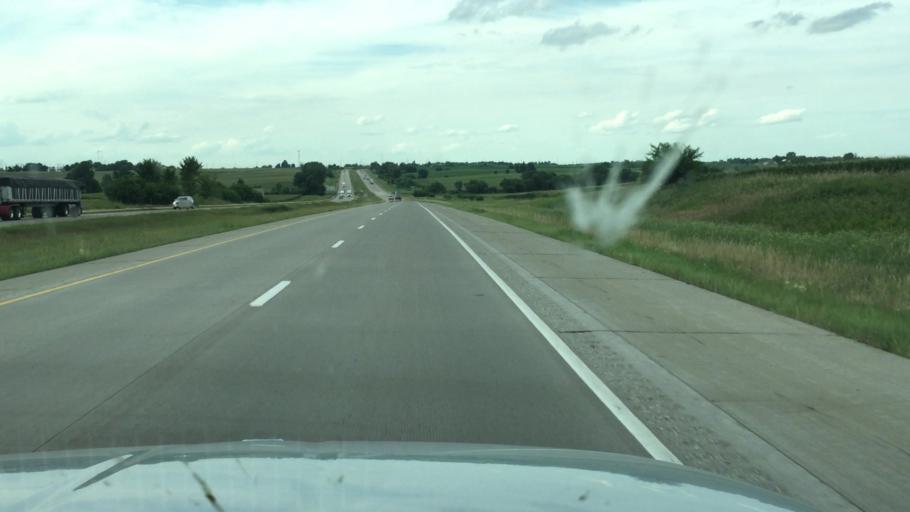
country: US
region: Iowa
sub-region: Scott County
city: Blue Grass
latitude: 41.5493
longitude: -90.6779
